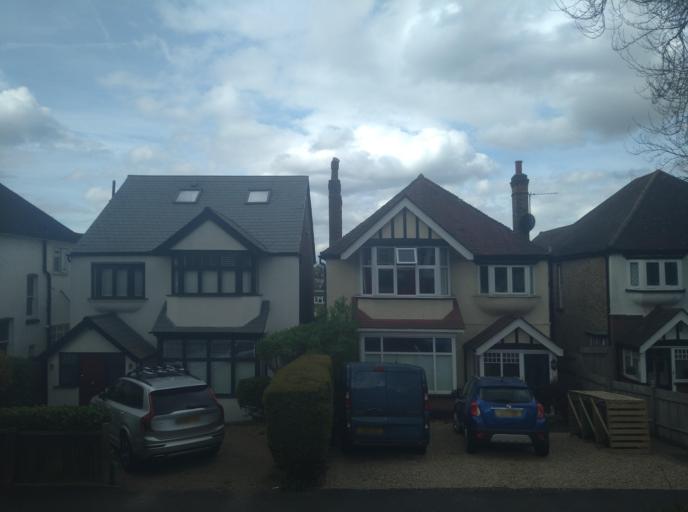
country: GB
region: England
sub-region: Greater London
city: Carshalton
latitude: 51.3548
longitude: -0.1711
